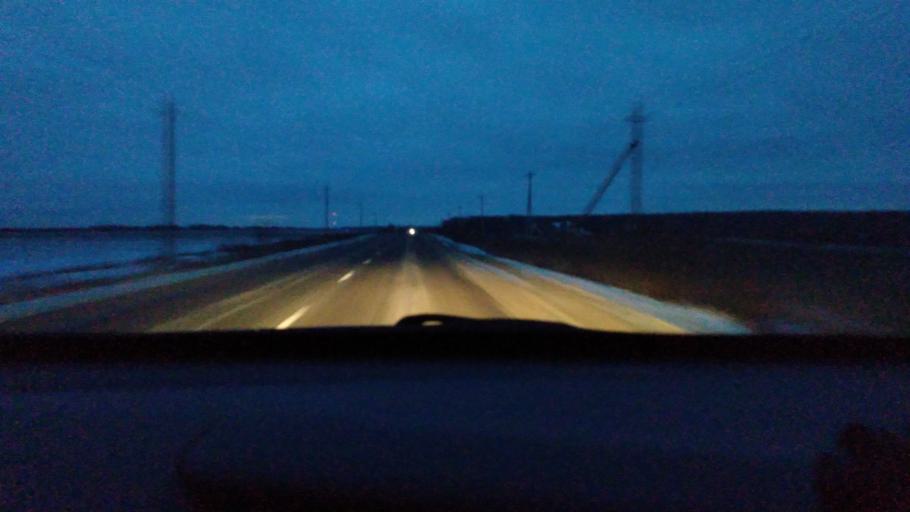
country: RU
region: Moskovskaya
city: Meshcherino
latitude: 55.2906
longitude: 38.3315
